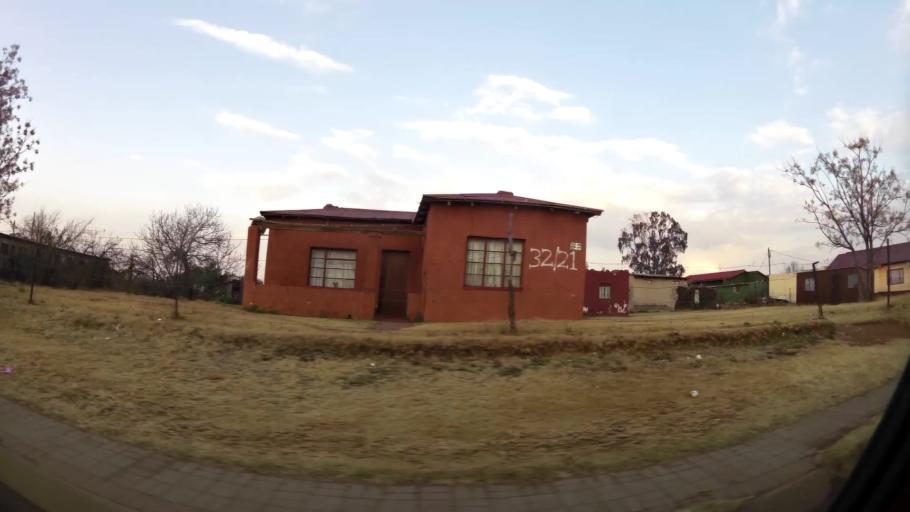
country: ZA
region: Gauteng
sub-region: City of Johannesburg Metropolitan Municipality
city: Orange Farm
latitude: -26.5489
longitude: 27.8415
